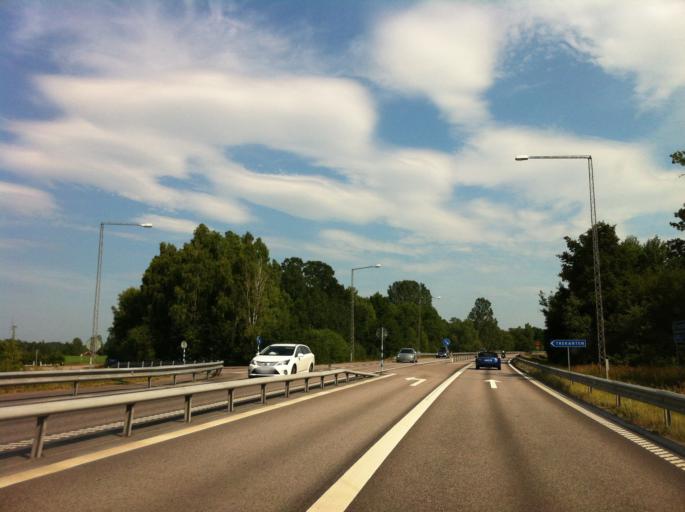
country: SE
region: Kalmar
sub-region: Kalmar Kommun
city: Trekanten
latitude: 56.7106
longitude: 16.0711
